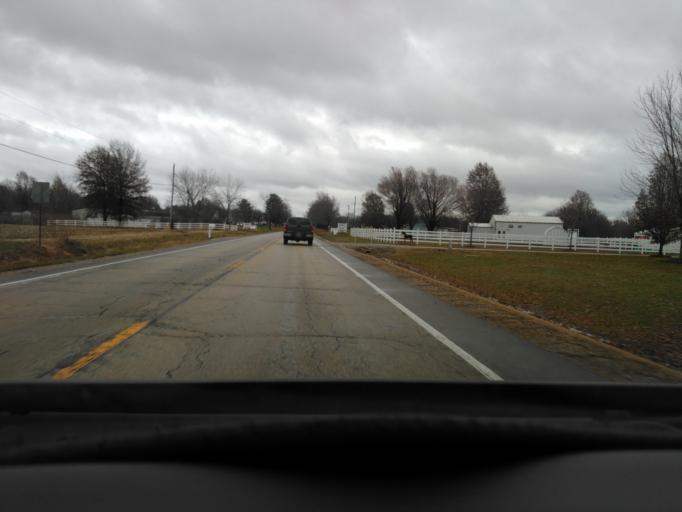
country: US
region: Illinois
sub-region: Effingham County
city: Altamont
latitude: 39.0516
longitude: -88.7596
